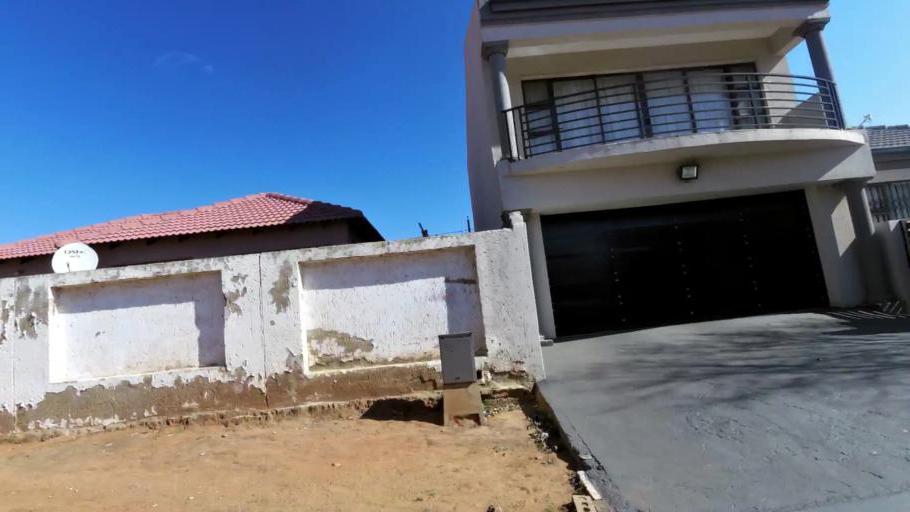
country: ZA
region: Gauteng
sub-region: City of Johannesburg Metropolitan Municipality
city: Johannesburg
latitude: -26.2486
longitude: 27.9844
